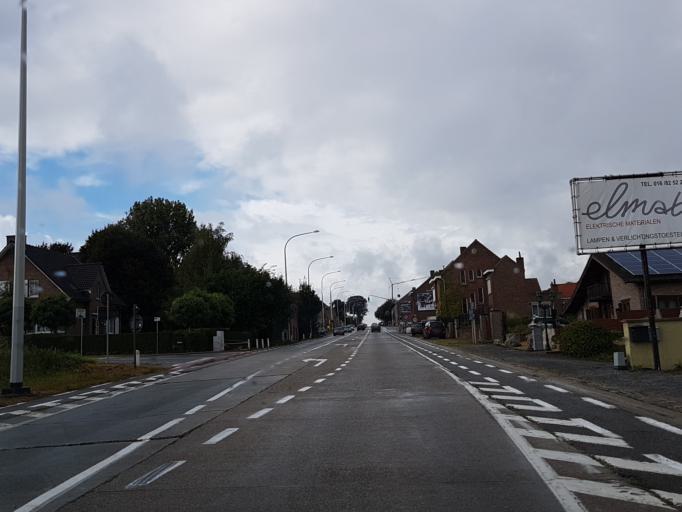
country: BE
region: Flanders
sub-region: Provincie Vlaams-Brabant
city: Hoegaarden
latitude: 50.8215
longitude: 4.8934
